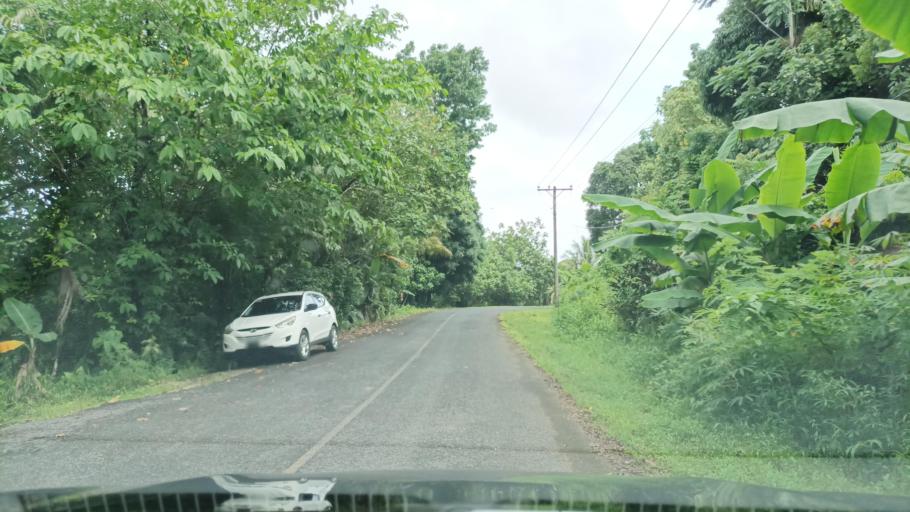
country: FM
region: Pohnpei
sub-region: Madolenihm Municipality
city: Madolenihm Municipality Government
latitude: 6.8300
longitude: 158.2984
